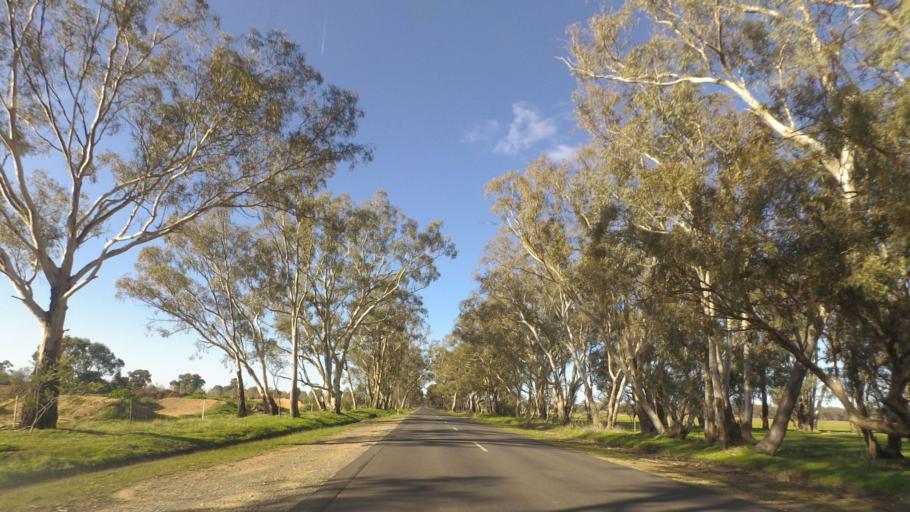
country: AU
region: Victoria
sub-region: Greater Bendigo
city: Epsom
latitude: -36.6610
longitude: 144.4610
